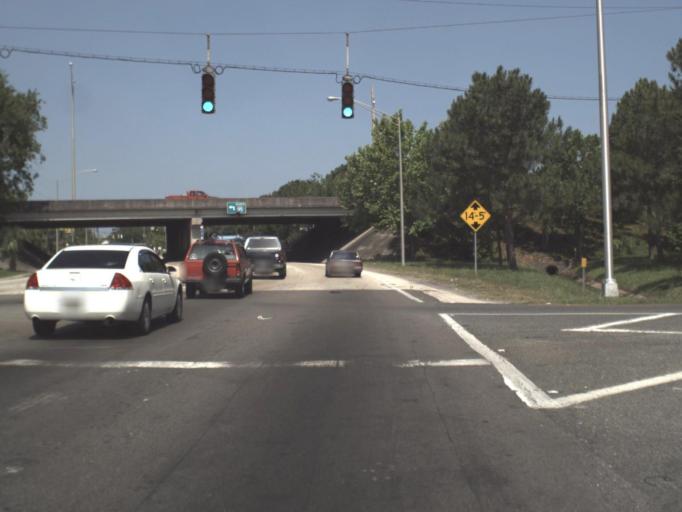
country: US
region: Florida
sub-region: Duval County
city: Jacksonville
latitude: 30.3648
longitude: -81.6676
